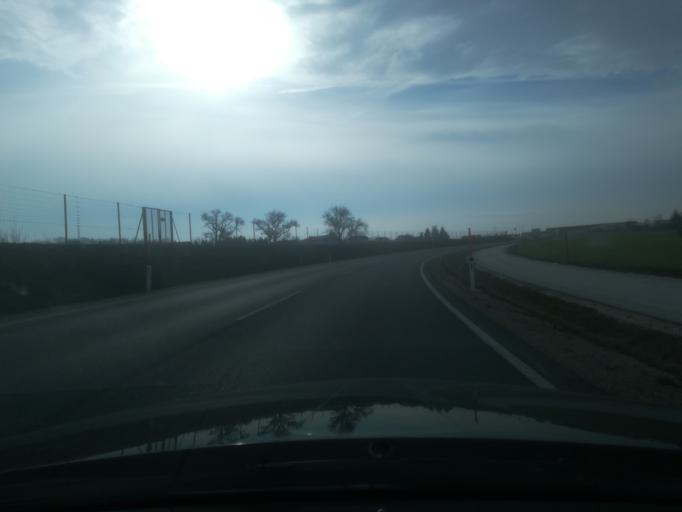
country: AT
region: Lower Austria
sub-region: Politischer Bezirk Amstetten
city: Ennsdorf
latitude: 48.2256
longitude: 14.5134
